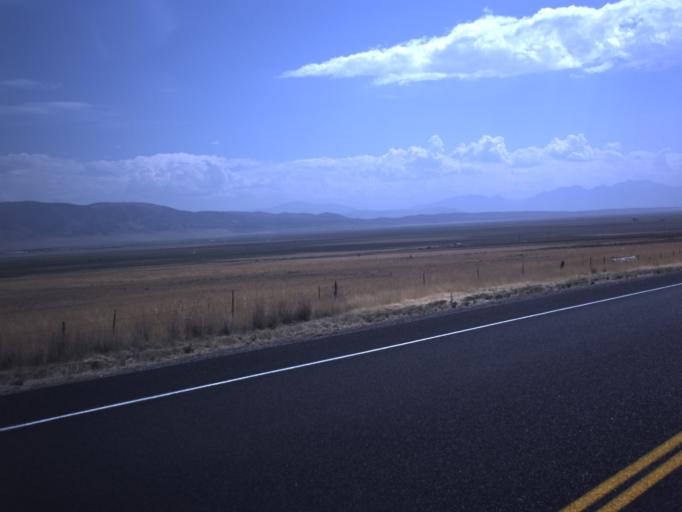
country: US
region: Utah
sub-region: Utah County
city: Eagle Mountain
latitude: 40.2999
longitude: -112.0996
